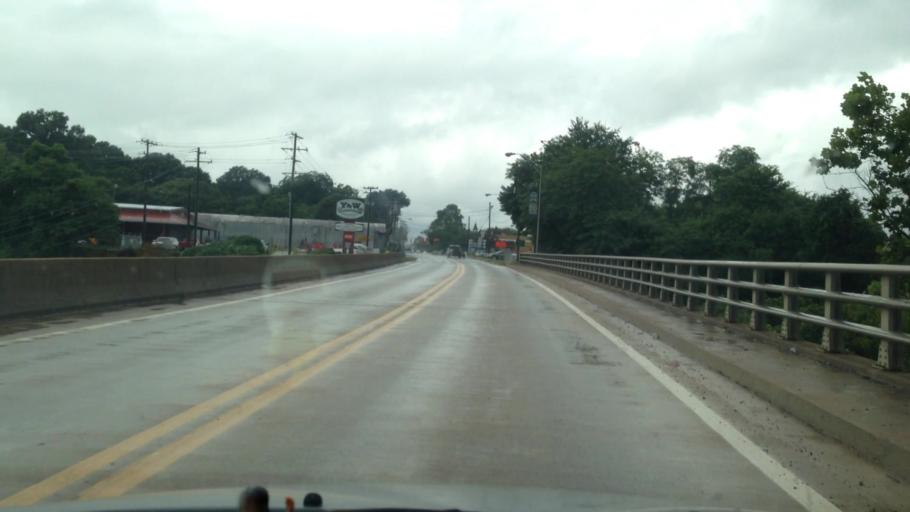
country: US
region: North Carolina
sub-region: Rockingham County
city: Madison
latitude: 36.3854
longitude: -79.9563
